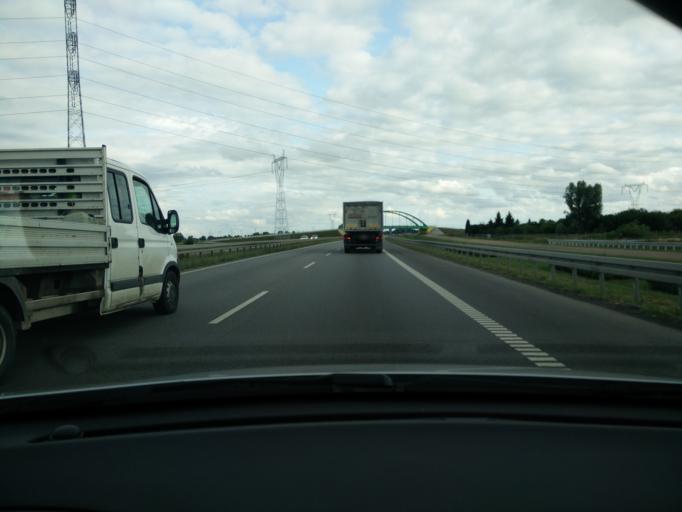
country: PL
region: Pomeranian Voivodeship
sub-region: Gdansk
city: Gdansk
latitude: 54.3362
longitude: 18.7020
